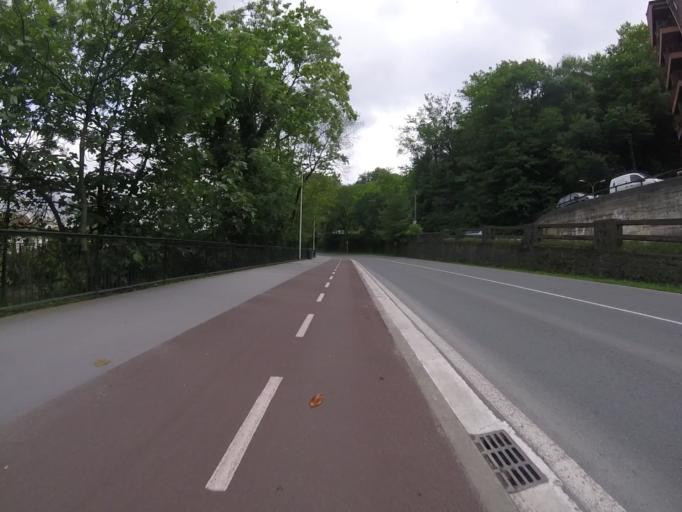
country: ES
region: Basque Country
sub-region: Provincia de Guipuzcoa
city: San Sebastian
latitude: 43.3063
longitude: -1.9661
